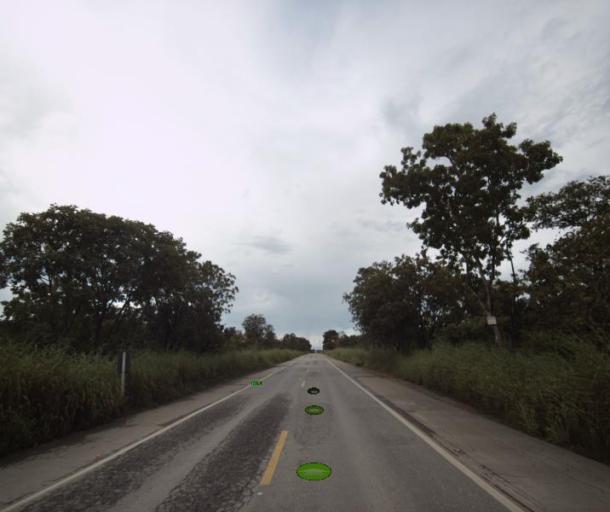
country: BR
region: Goias
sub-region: Porangatu
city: Porangatu
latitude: -13.5861
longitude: -49.0415
